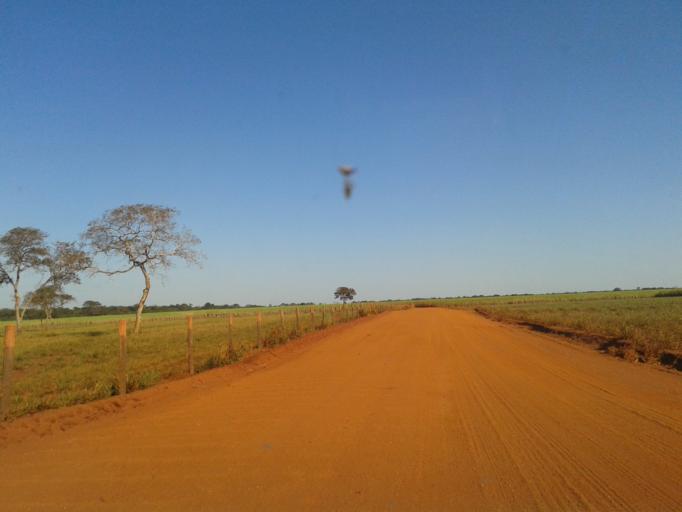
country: BR
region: Minas Gerais
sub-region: Santa Vitoria
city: Santa Vitoria
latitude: -18.8526
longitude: -50.0529
